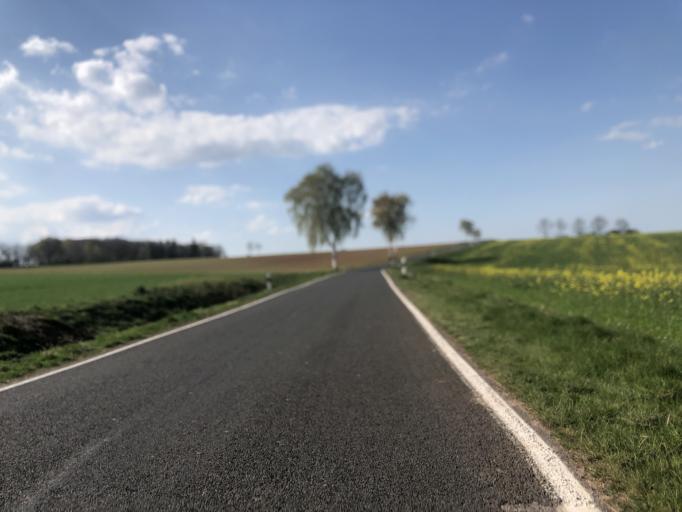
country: DE
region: North Rhine-Westphalia
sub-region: Regierungsbezirk Koln
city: Kall
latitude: 50.6144
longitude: 6.5640
